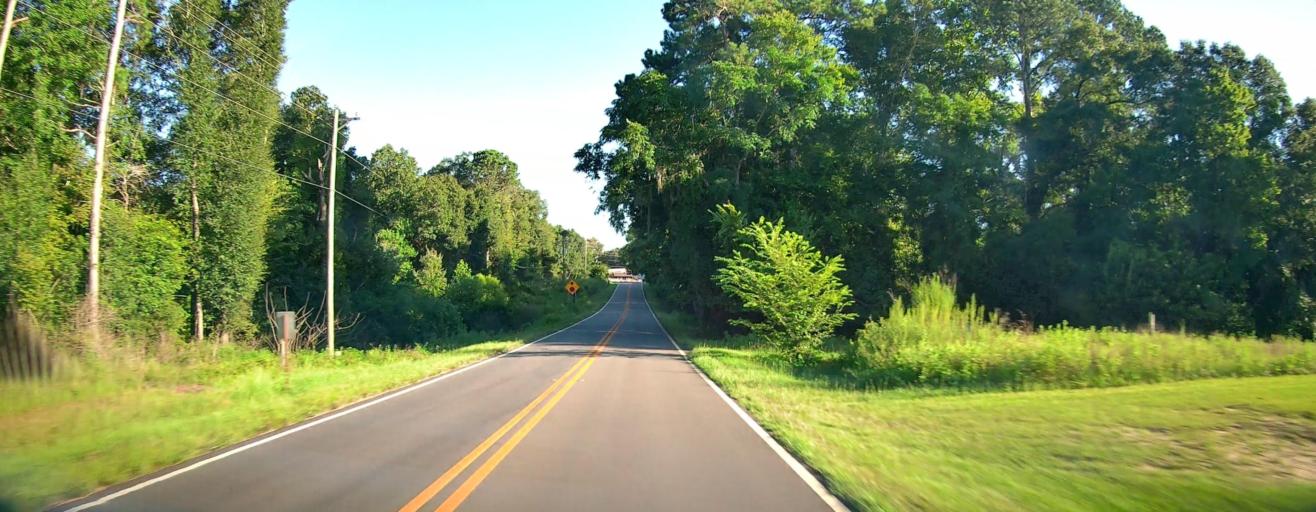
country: US
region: Georgia
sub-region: Pulaski County
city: Hawkinsville
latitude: 32.2885
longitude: -83.4490
